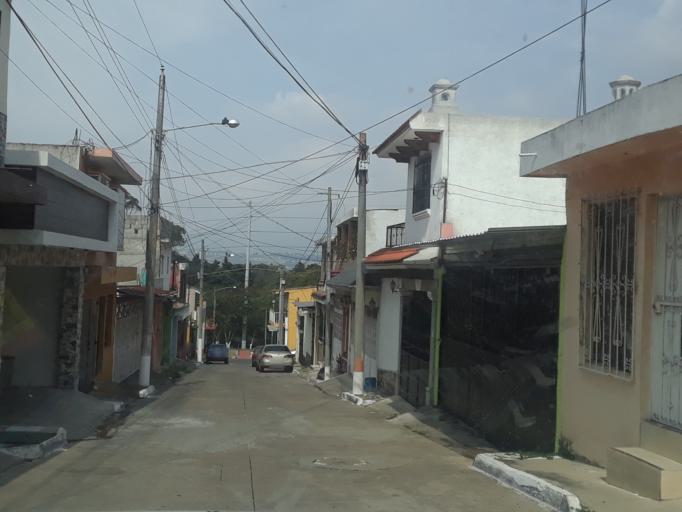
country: GT
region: Guatemala
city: Petapa
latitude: 14.5351
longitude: -90.5556
